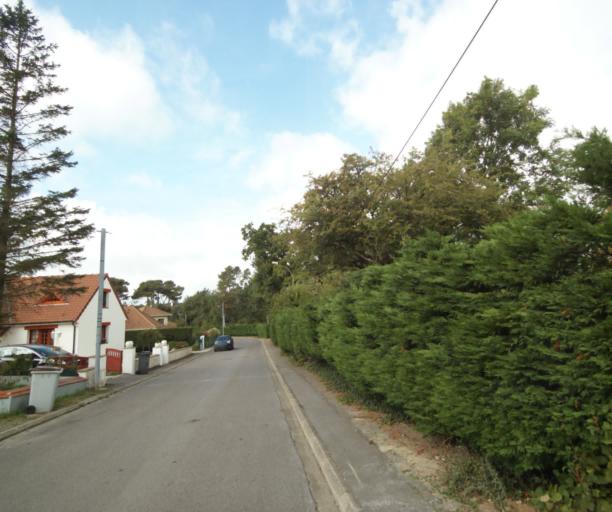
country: FR
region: Nord-Pas-de-Calais
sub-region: Departement du Pas-de-Calais
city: Etaples
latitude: 50.5286
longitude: 1.6350
